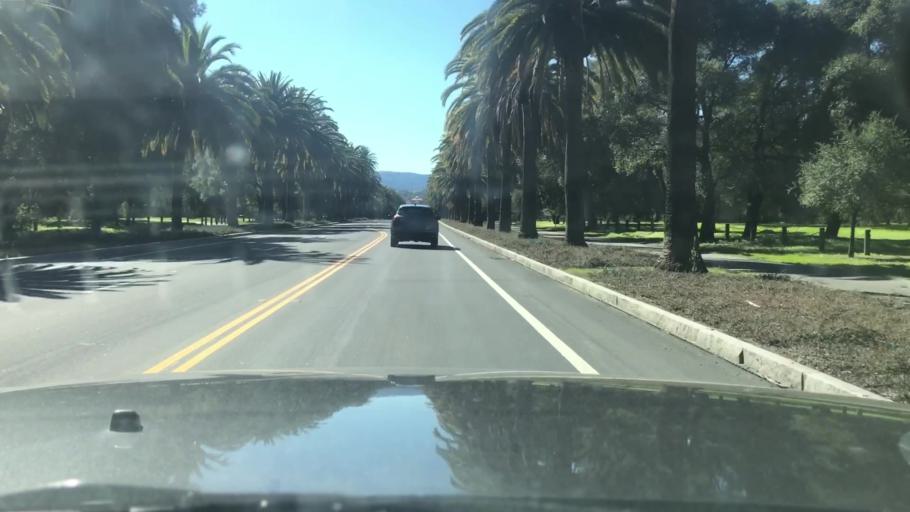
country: US
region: California
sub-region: Santa Clara County
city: Stanford
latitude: 37.4370
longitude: -122.1672
